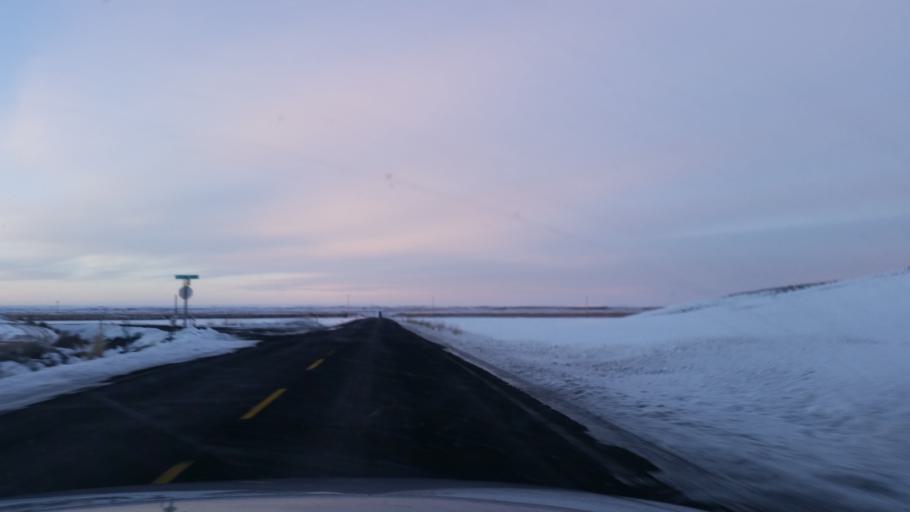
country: US
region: Washington
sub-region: Spokane County
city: Cheney
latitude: 47.2065
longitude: -117.8877
